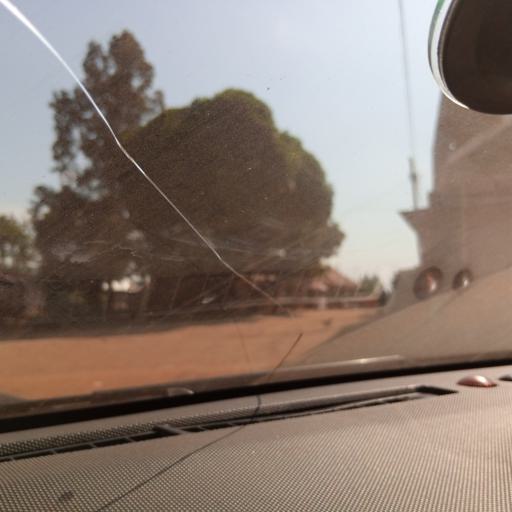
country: UG
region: Central Region
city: Masaka
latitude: -0.3276
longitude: 31.7311
